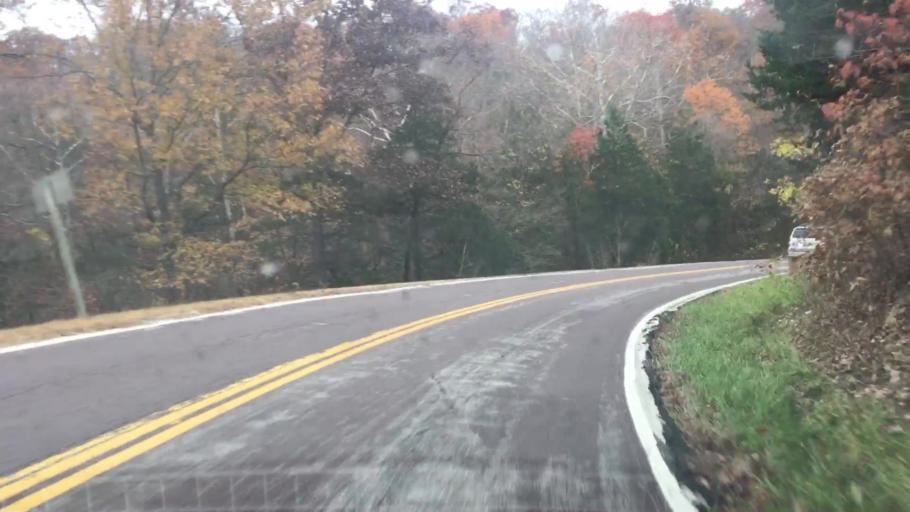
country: US
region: Missouri
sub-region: Callaway County
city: Fulton
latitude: 38.7906
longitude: -91.7551
